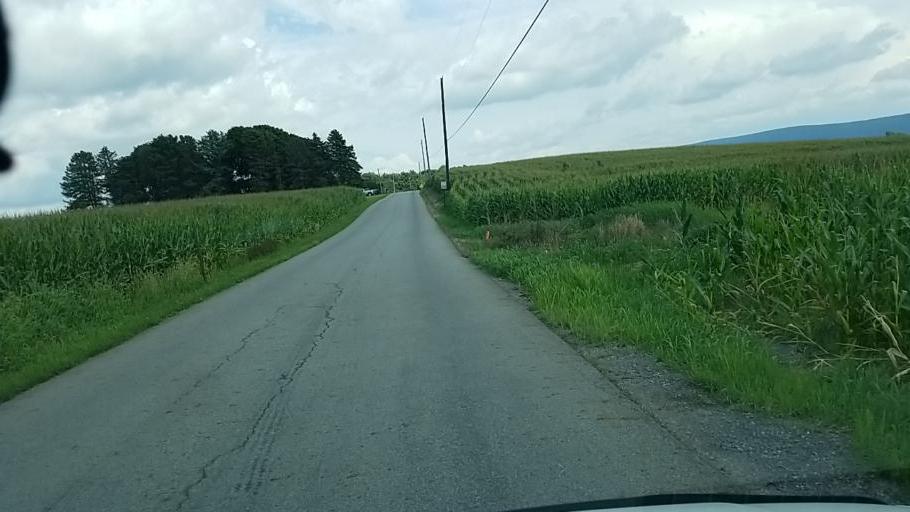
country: US
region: Pennsylvania
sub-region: Dauphin County
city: Elizabethville
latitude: 40.6131
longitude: -76.8158
